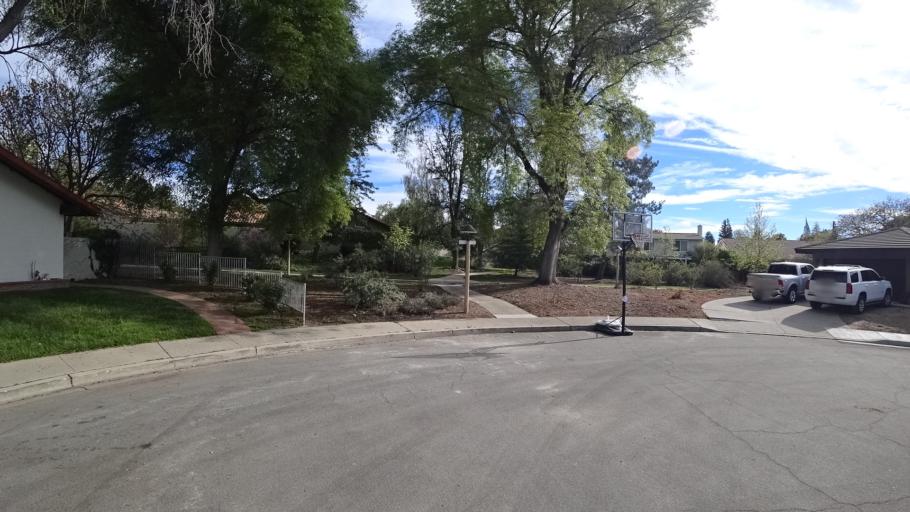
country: US
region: California
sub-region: Ventura County
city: Thousand Oaks
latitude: 34.1542
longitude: -118.8405
